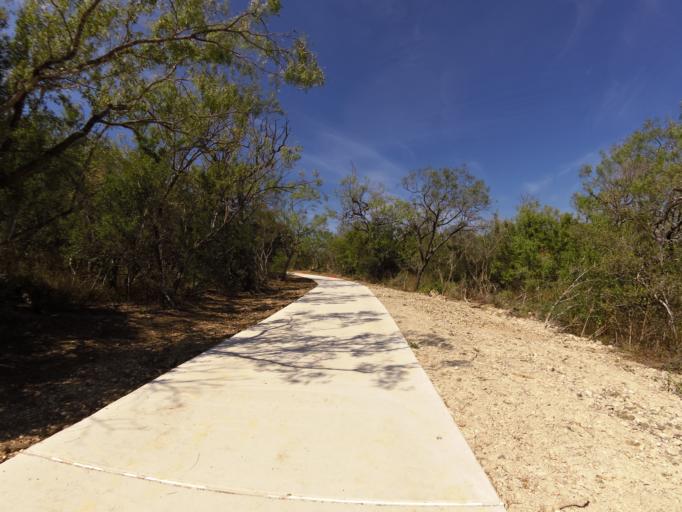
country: US
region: Texas
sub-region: Bexar County
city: San Antonio
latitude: 29.3849
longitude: -98.4330
